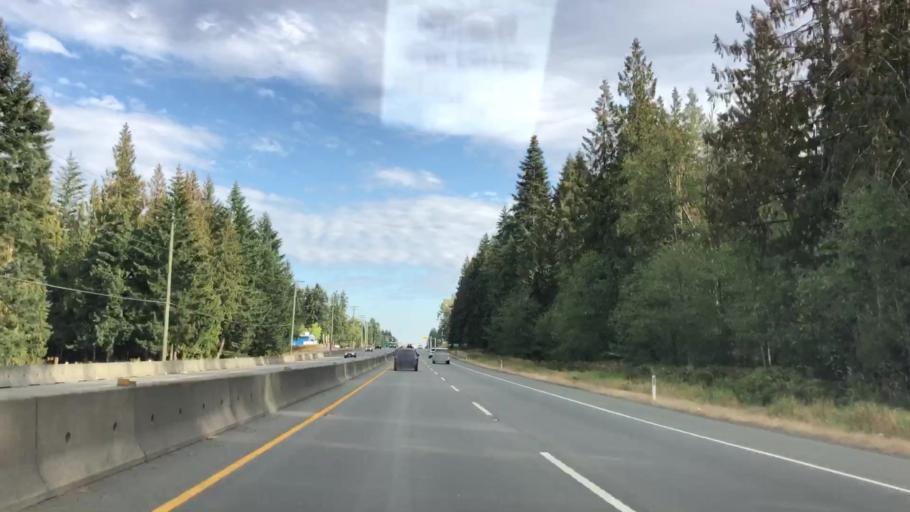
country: CA
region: British Columbia
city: Duncan
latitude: 48.6996
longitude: -123.5968
